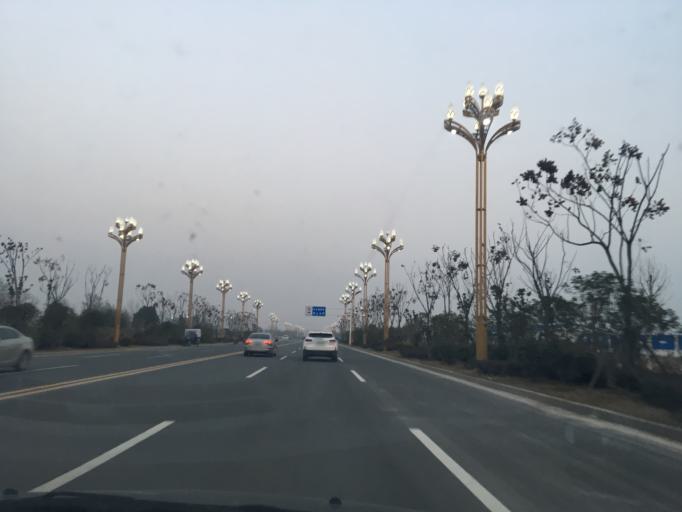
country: CN
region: Hubei
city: Macheng
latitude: 31.1608
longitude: 115.0223
